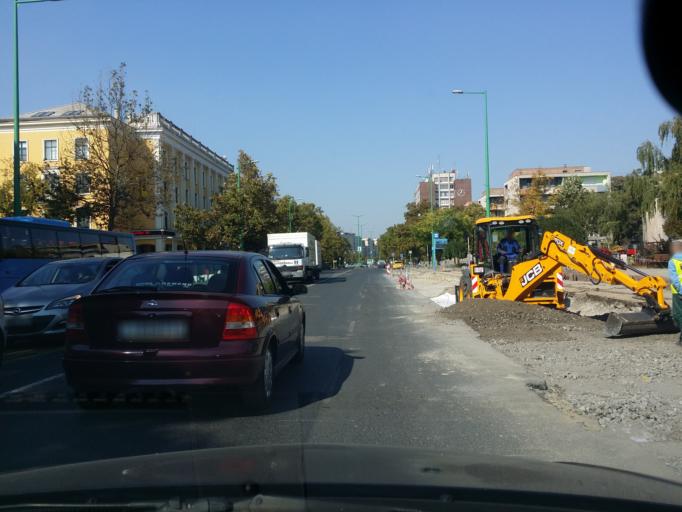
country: HU
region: Fejer
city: Dunaujvaros
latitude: 46.9631
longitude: 18.9415
